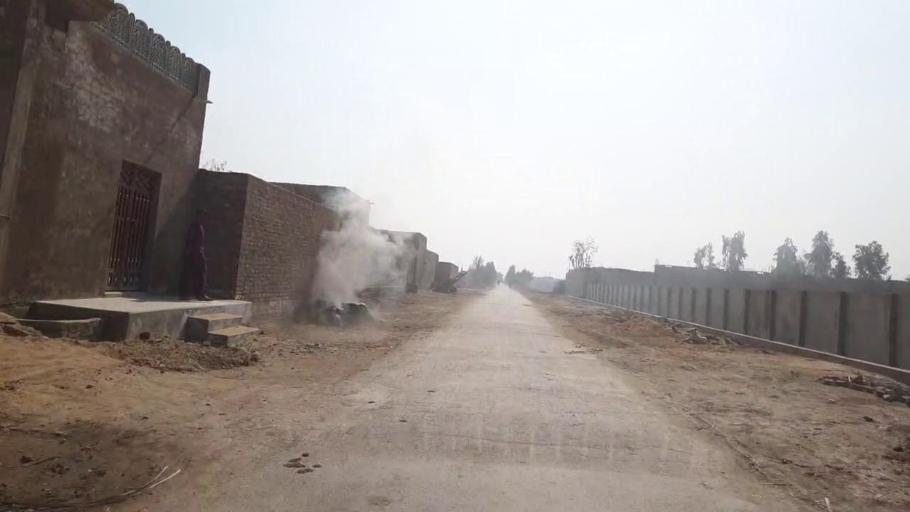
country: PK
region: Sindh
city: Bhit Shah
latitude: 25.7020
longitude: 68.5439
